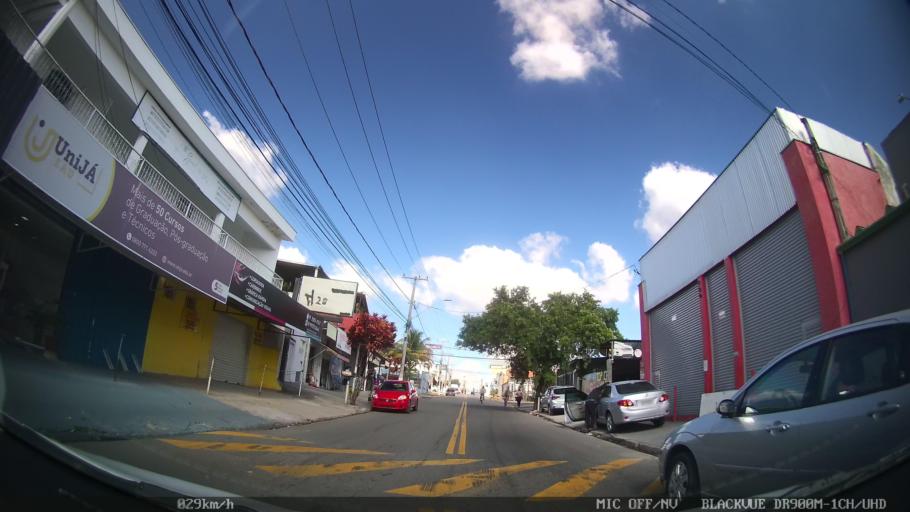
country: BR
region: Sao Paulo
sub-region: Hortolandia
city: Hortolandia
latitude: -22.8794
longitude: -47.1998
